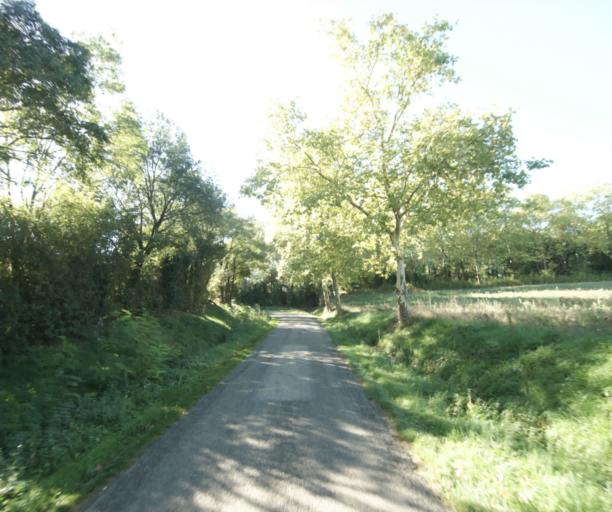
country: FR
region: Midi-Pyrenees
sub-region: Departement du Gers
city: Eauze
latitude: 43.8146
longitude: 0.1620
